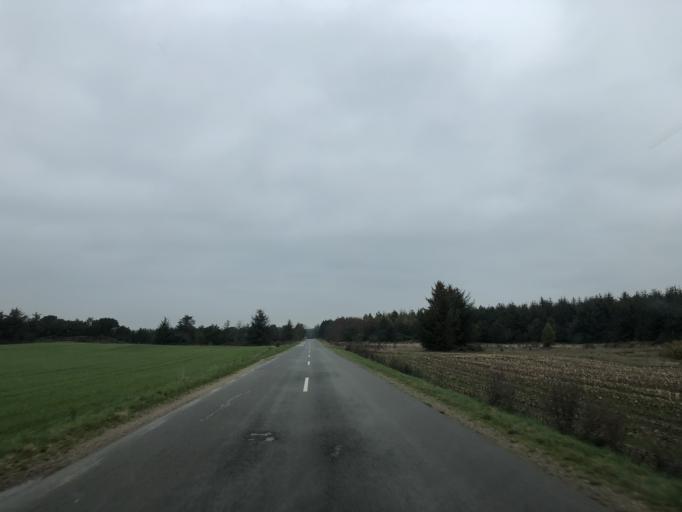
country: DK
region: Central Jutland
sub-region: Holstebro Kommune
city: Ulfborg
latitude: 56.2365
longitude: 8.3834
